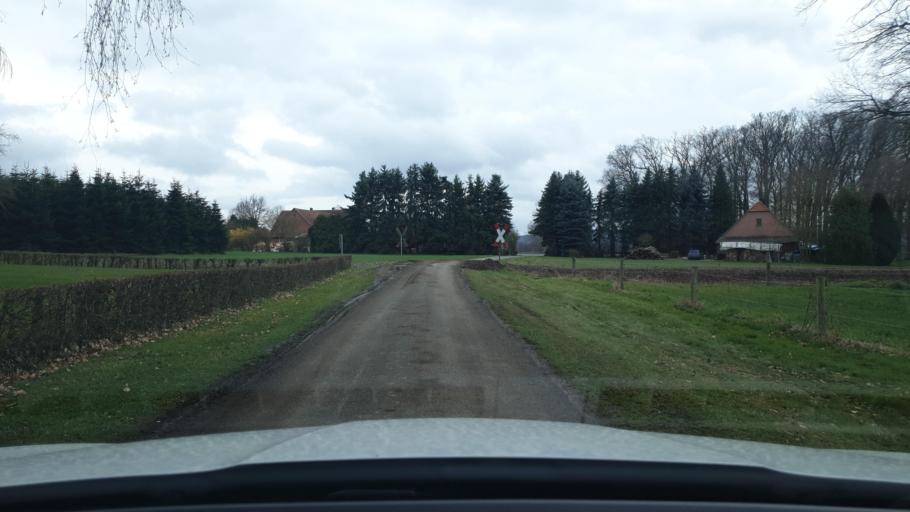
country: DE
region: North Rhine-Westphalia
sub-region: Regierungsbezirk Detmold
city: Hille
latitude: 52.3288
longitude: 8.7732
